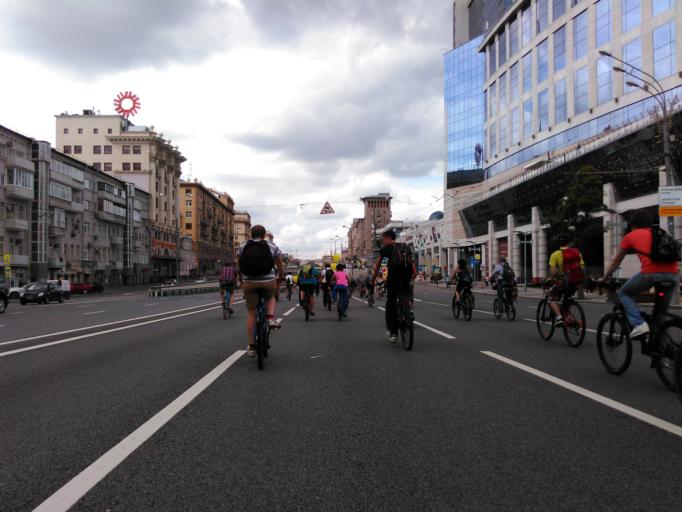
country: RU
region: Moskovskaya
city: Dorogomilovo
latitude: 55.7497
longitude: 37.5829
